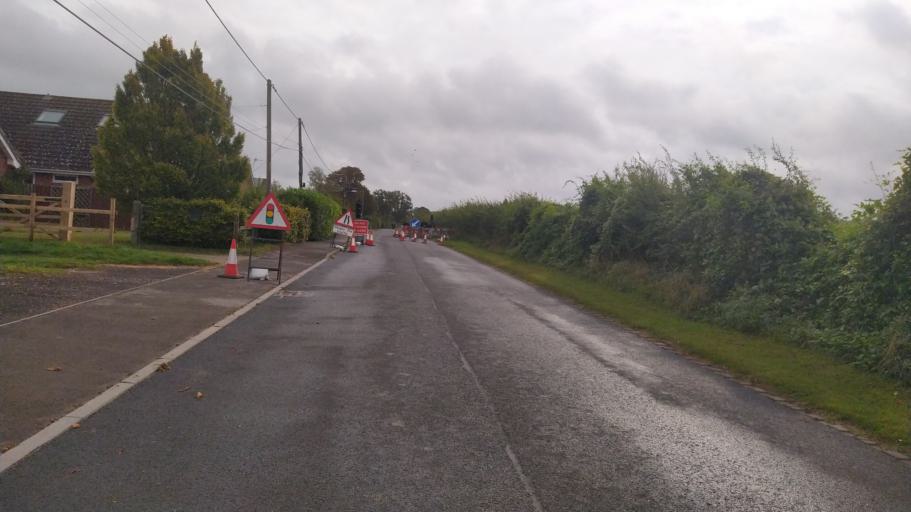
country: GB
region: England
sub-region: Wiltshire
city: Allington
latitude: 51.1184
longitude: -1.7234
